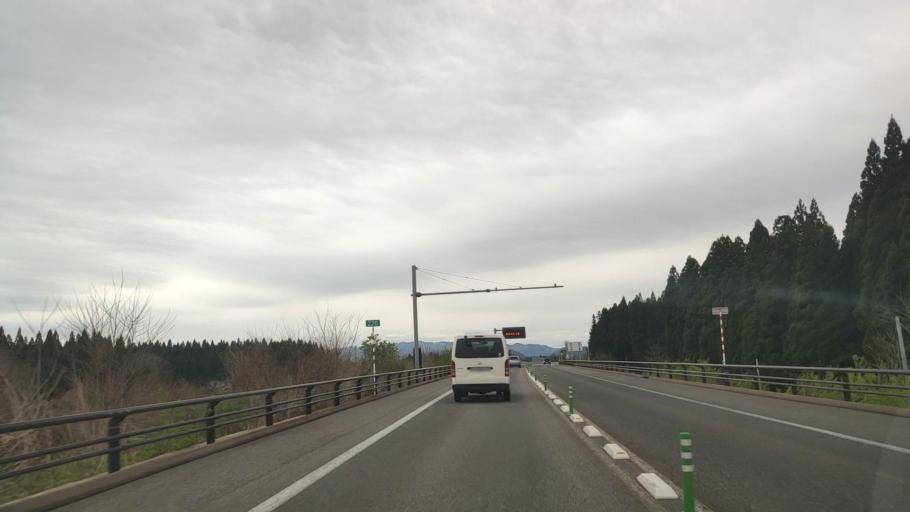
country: JP
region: Akita
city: Odate
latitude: 40.3076
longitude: 140.5733
